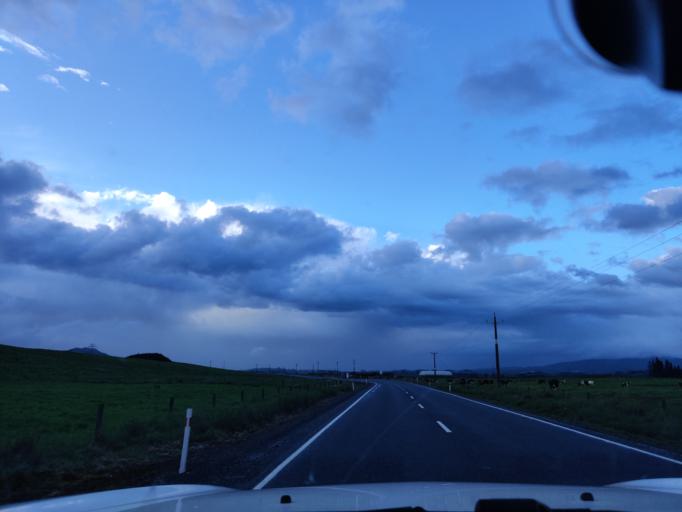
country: NZ
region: Waikato
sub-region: South Waikato District
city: Tokoroa
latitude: -38.3897
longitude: 175.7809
